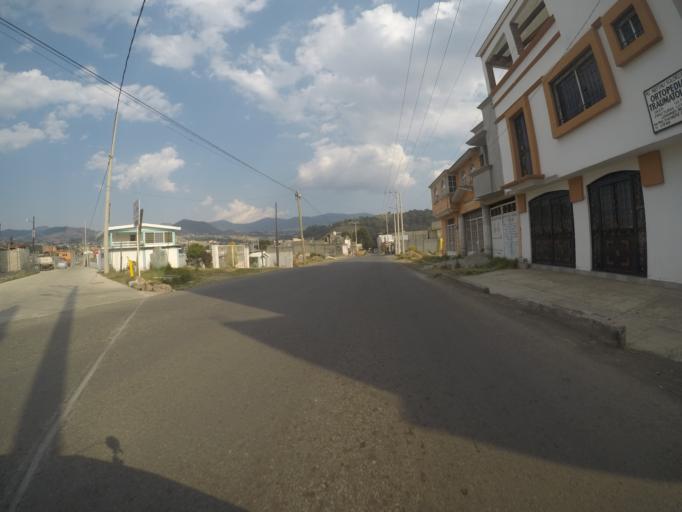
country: MX
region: Mexico
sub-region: Xalatlaco
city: Techichili
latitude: 19.1733
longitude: -99.4190
